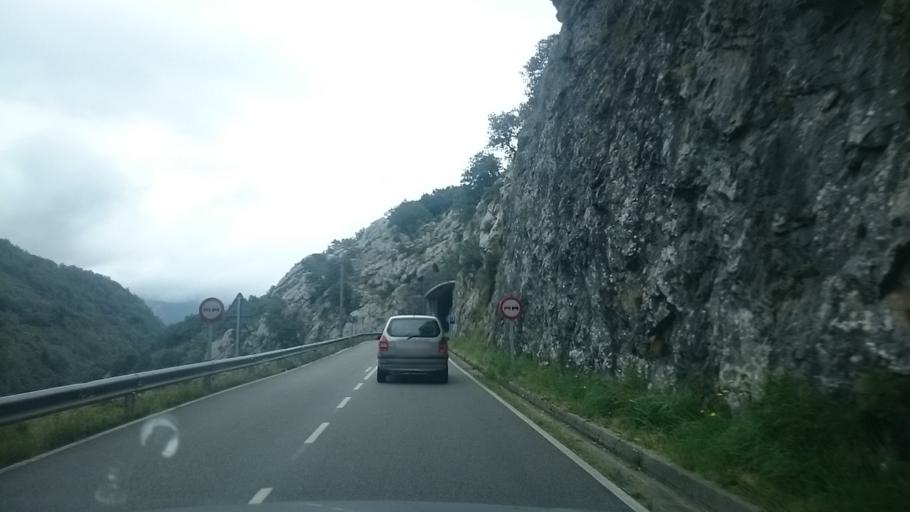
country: ES
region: Asturias
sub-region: Province of Asturias
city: Carrena
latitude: 43.2892
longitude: -4.8269
